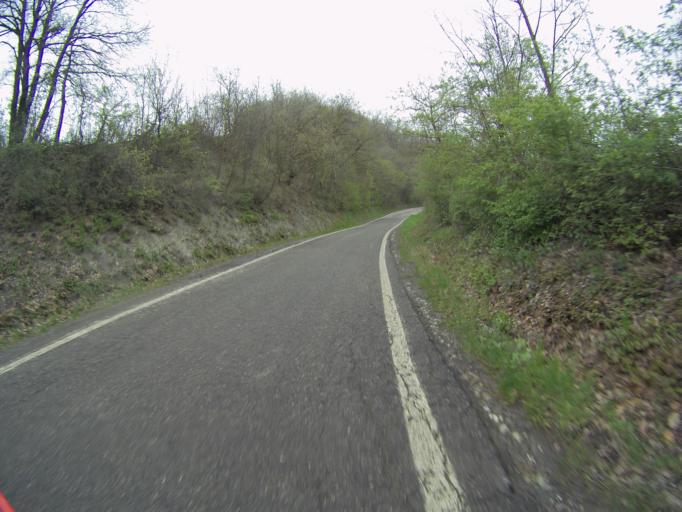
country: IT
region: Emilia-Romagna
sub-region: Provincia di Reggio Emilia
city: San Polo d'Enza
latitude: 44.6117
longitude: 10.4527
